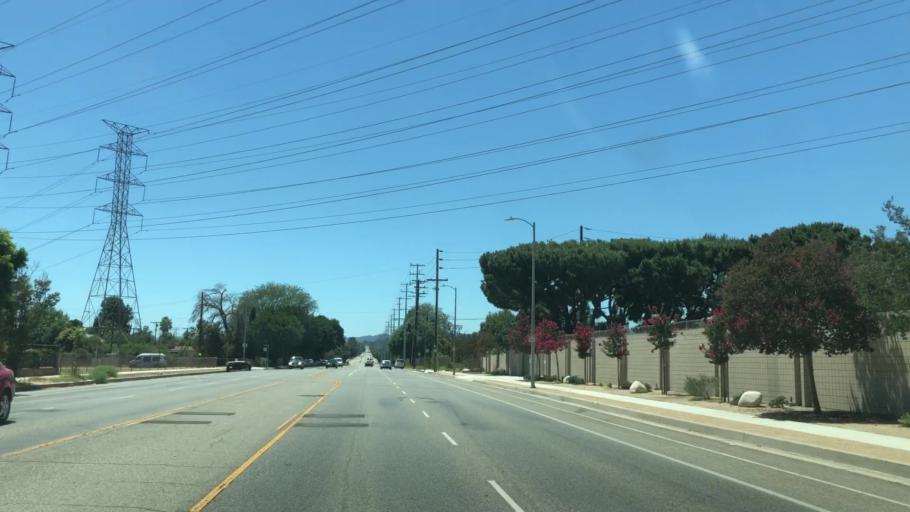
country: US
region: California
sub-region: Los Angeles County
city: San Fernando
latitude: 34.2792
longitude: -118.4790
